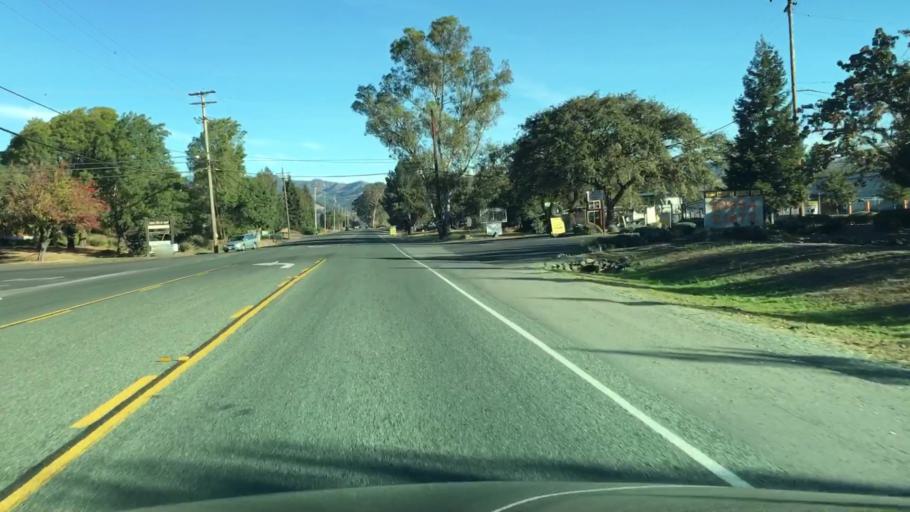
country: US
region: California
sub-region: Sonoma County
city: Sonoma
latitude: 38.2600
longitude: -122.4404
